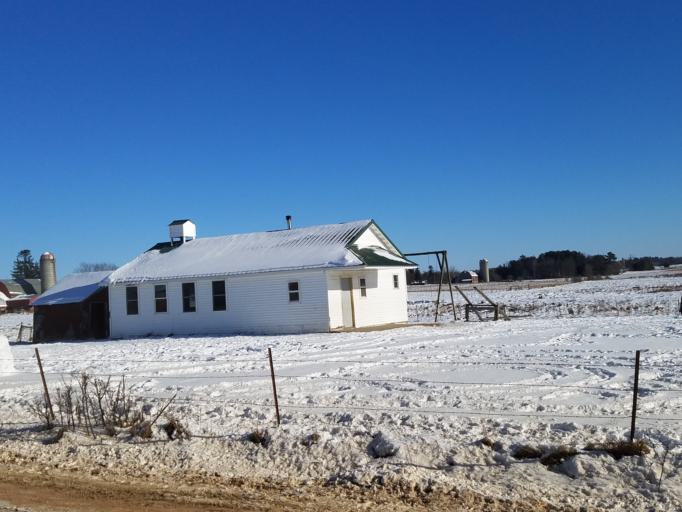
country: US
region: Wisconsin
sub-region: Clark County
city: Neillsville
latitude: 44.5653
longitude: -90.4164
